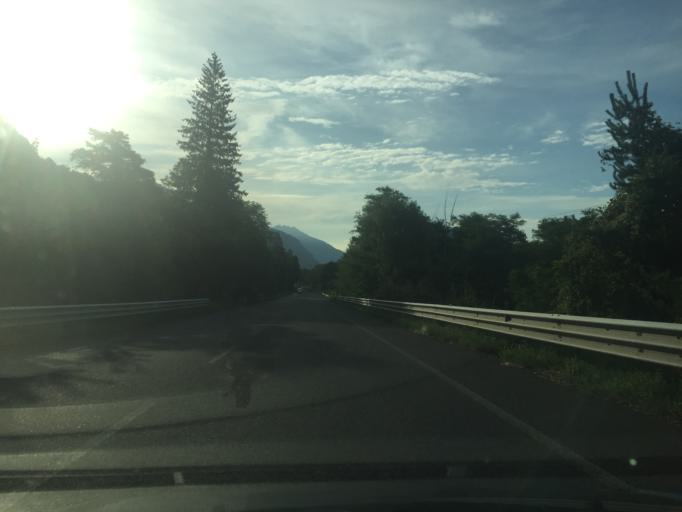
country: IT
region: Friuli Venezia Giulia
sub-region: Provincia di Udine
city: Chiaulis
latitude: 46.4096
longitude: 12.9686
